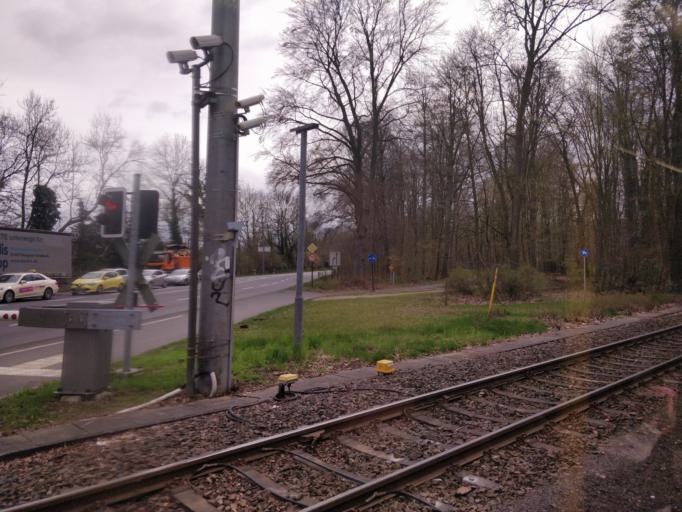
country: DE
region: North Rhine-Westphalia
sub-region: Regierungsbezirk Koln
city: Neuehrenfeld
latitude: 50.9237
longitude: 6.8904
